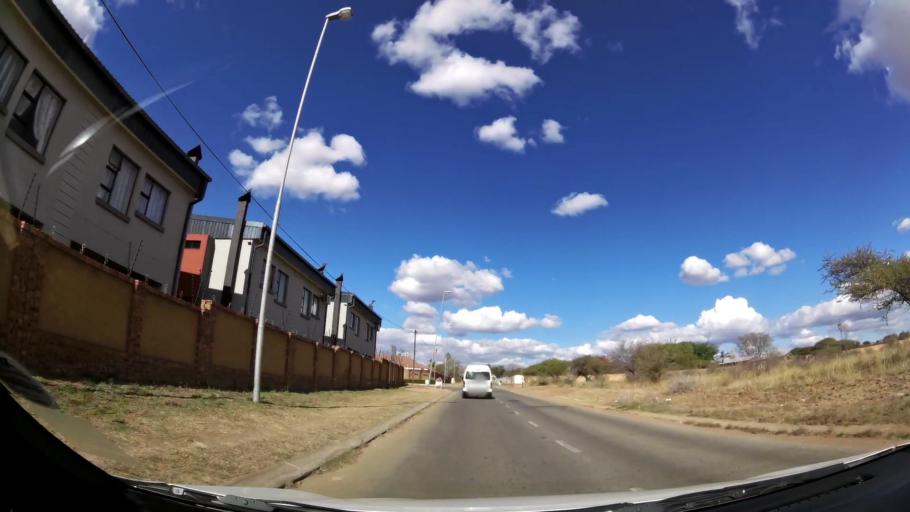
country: ZA
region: Limpopo
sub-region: Capricorn District Municipality
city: Polokwane
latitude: -23.8763
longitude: 29.4832
